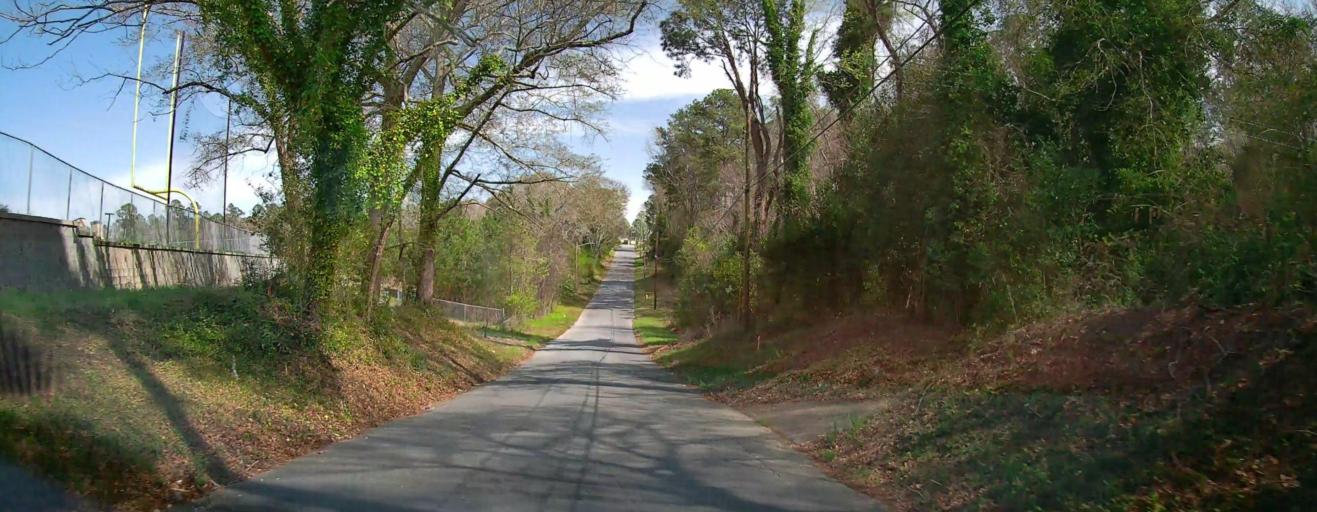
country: US
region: Georgia
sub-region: Bibb County
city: Macon
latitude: 32.8640
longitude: -83.6212
